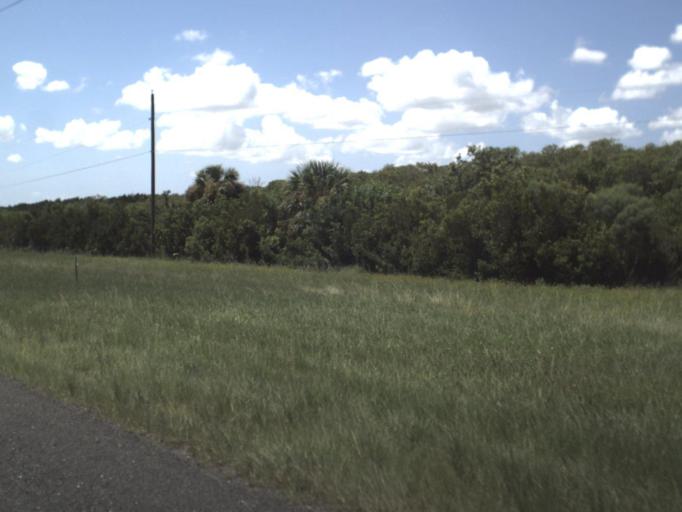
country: US
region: Florida
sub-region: Pinellas County
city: Feather Sound
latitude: 27.8907
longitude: -82.6390
